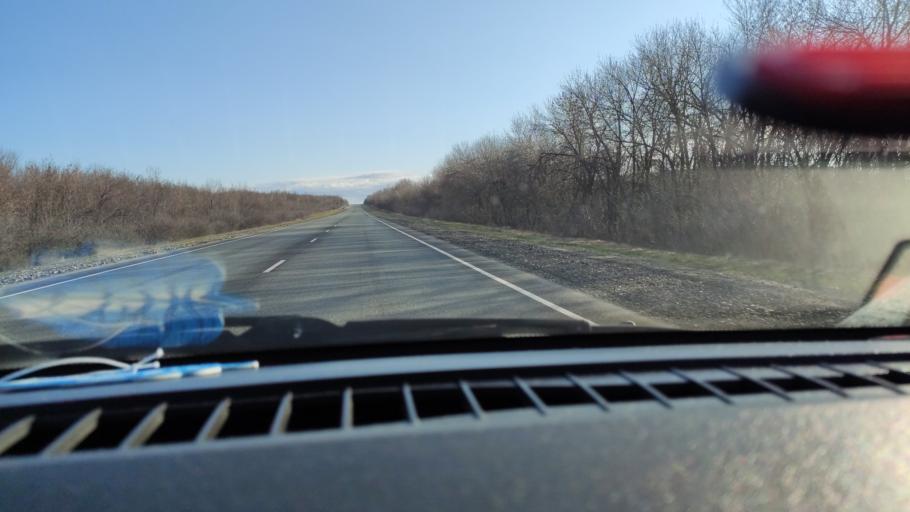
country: RU
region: Saratov
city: Khvalynsk
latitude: 52.6146
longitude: 48.1640
